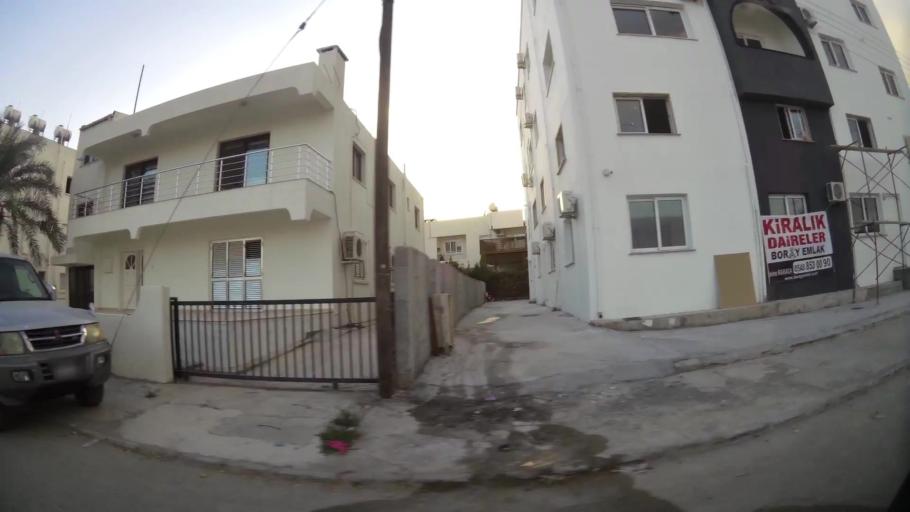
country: CY
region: Lefkosia
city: Nicosia
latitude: 35.2009
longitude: 33.3727
